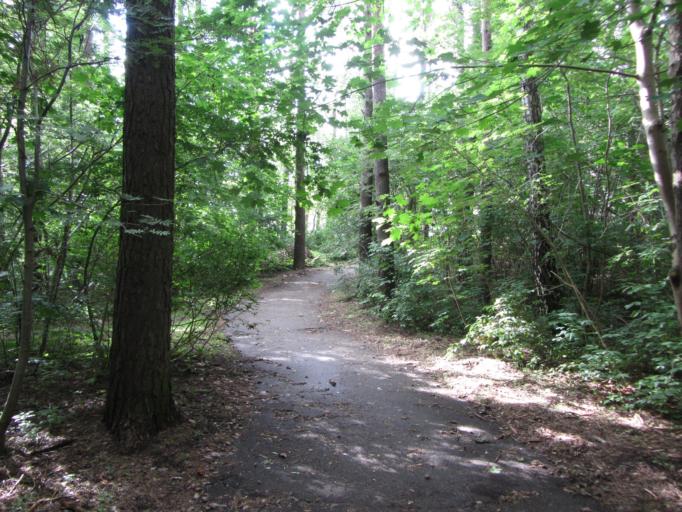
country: LT
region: Vilnius County
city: Lazdynai
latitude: 54.6826
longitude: 25.2029
